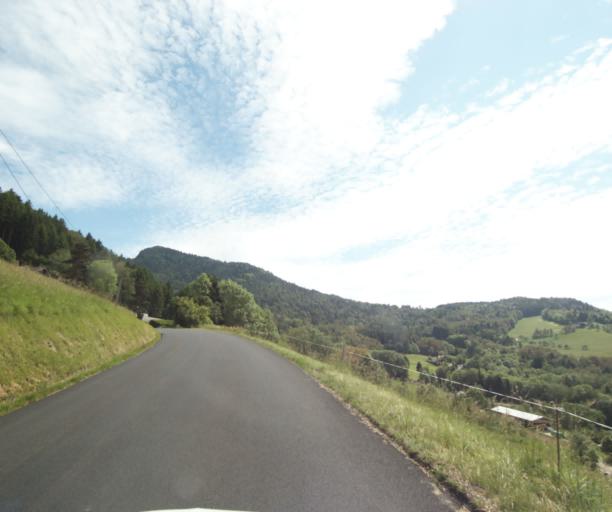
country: FR
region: Rhone-Alpes
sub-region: Departement de la Haute-Savoie
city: Perrignier
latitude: 46.2924
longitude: 6.4753
